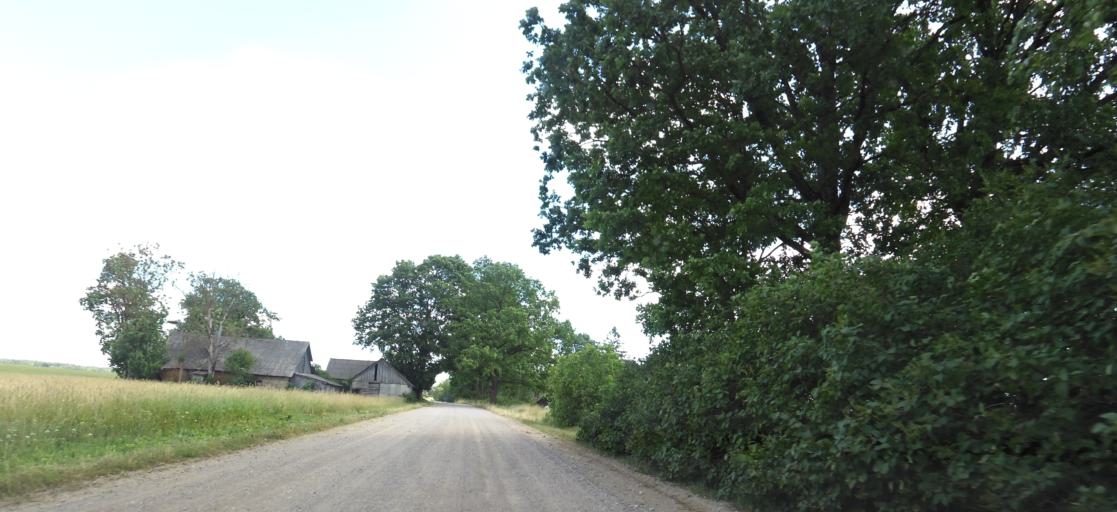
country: LT
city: Vabalninkas
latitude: 56.0276
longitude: 24.9128
